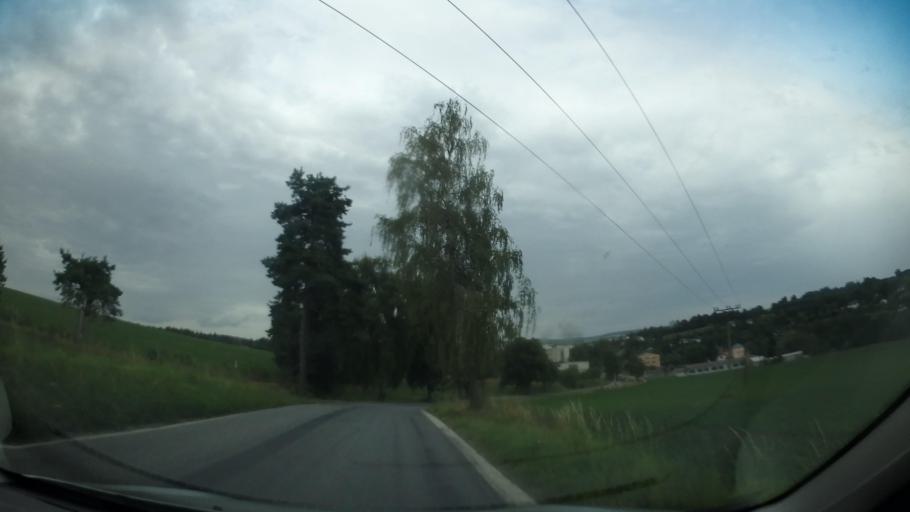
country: CZ
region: Vysocina
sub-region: Okres Zd'ar nad Sazavou
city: Nove Mesto na Morave
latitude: 49.5503
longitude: 16.0684
